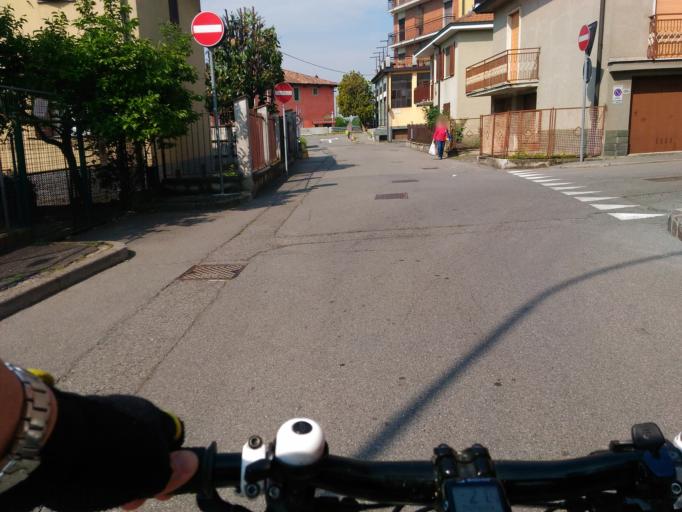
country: IT
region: Lombardy
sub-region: Provincia di Lodi
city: Sordio
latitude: 45.3391
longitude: 9.3657
